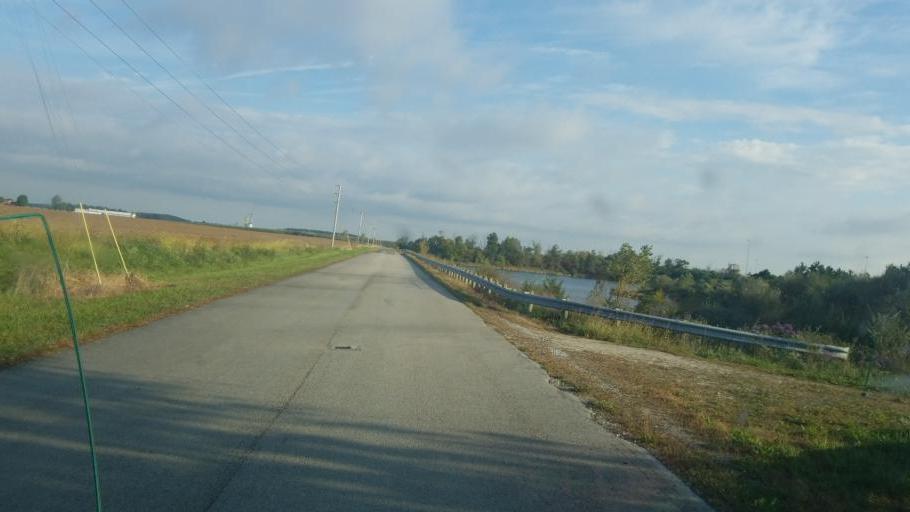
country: US
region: Ohio
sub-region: Wyandot County
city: Upper Sandusky
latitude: 40.8526
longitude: -83.3236
